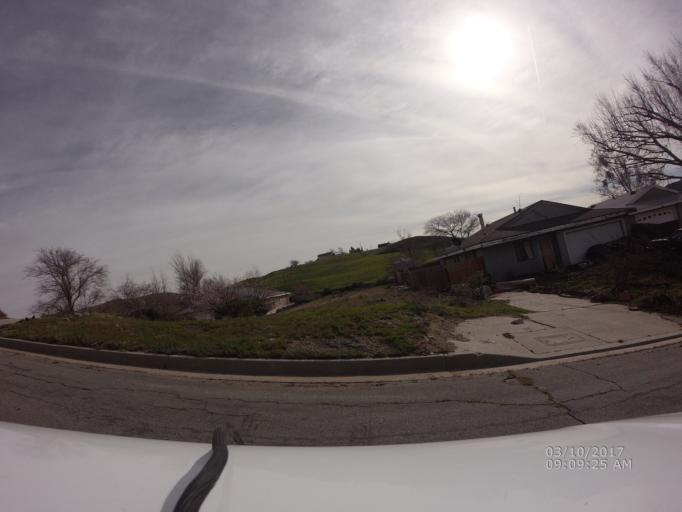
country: US
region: California
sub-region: Los Angeles County
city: Green Valley
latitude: 34.6554
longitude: -118.3841
